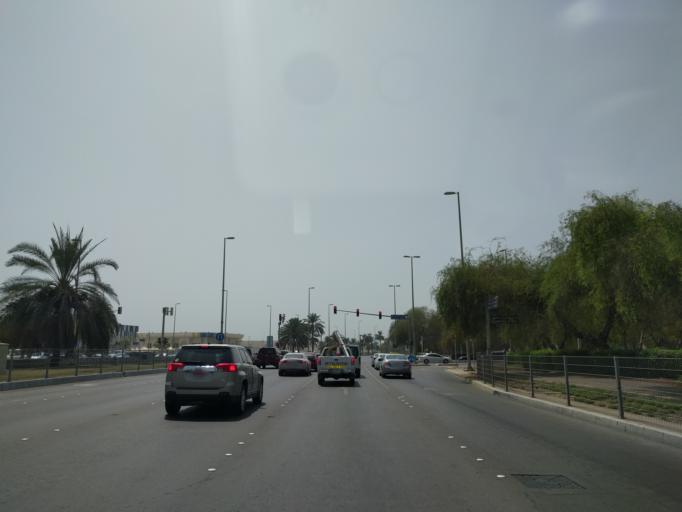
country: AE
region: Abu Dhabi
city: Abu Dhabi
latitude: 24.4413
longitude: 54.4079
